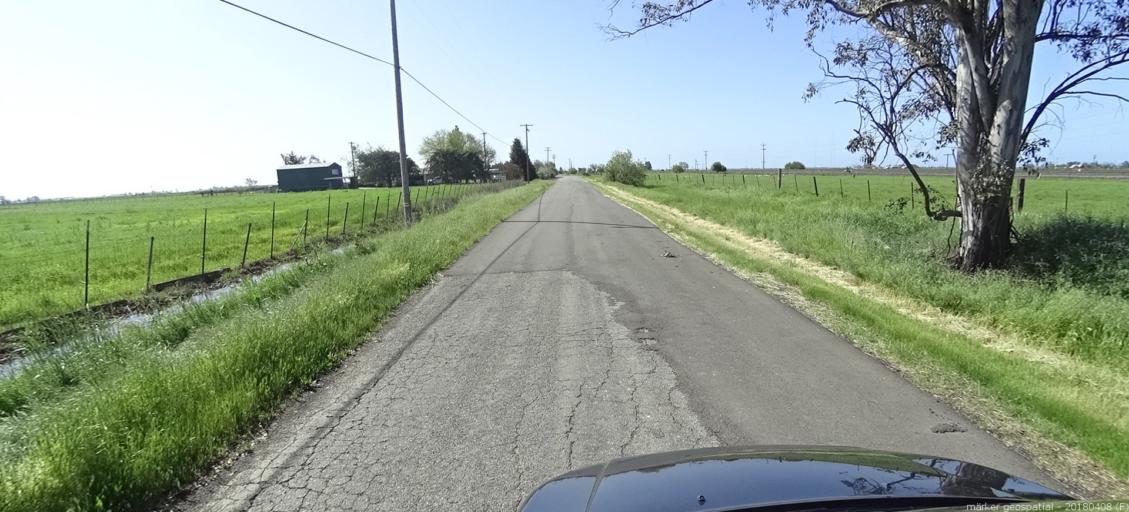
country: US
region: California
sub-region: Sacramento County
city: Laguna
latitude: 38.3386
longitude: -121.4452
